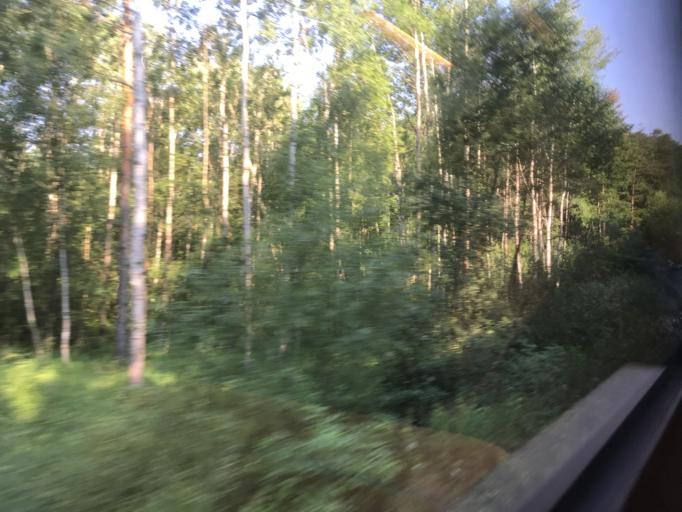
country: CZ
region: Jihocesky
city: Plana nad Luznici
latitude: 49.3284
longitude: 14.7151
